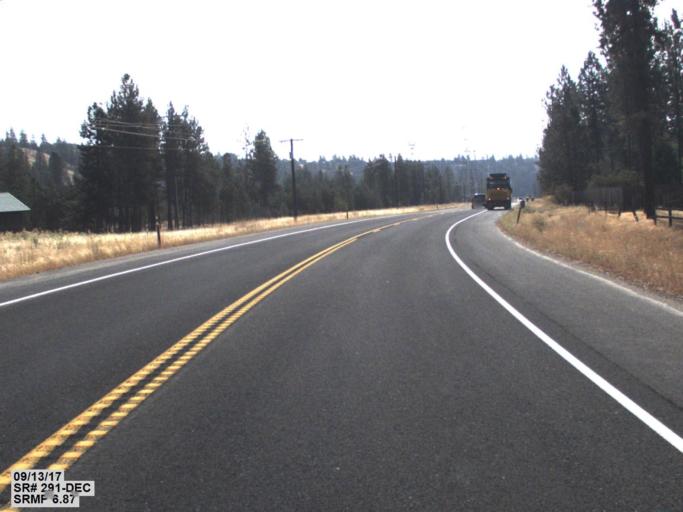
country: US
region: Washington
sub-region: Spokane County
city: Fairwood
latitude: 47.7580
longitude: -117.5199
